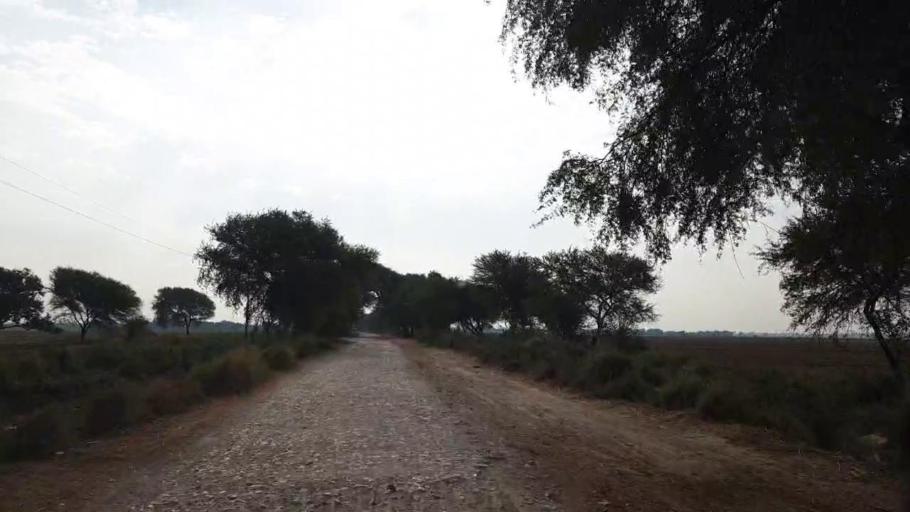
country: PK
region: Sindh
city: Tando Muhammad Khan
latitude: 25.0300
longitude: 68.4411
